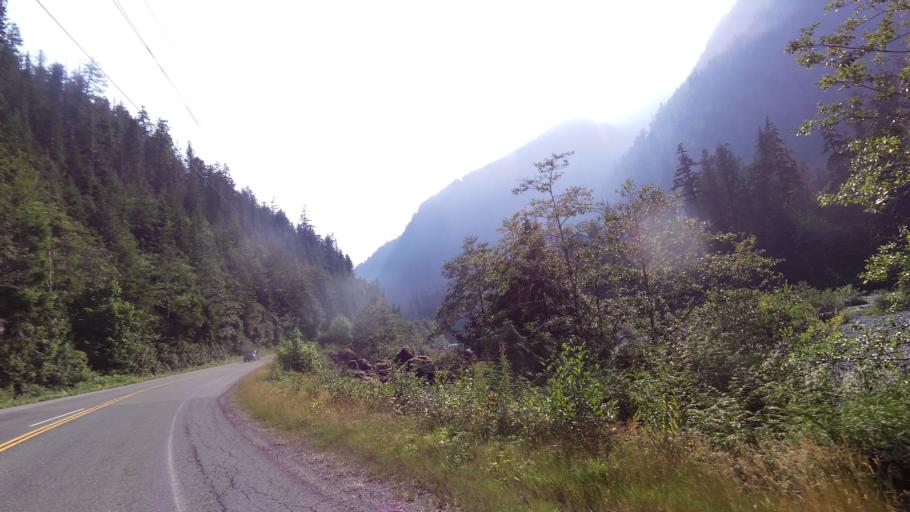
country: CA
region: British Columbia
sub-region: Regional District of Alberni-Clayoquot
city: Ucluelet
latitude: 49.2228
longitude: -125.3649
